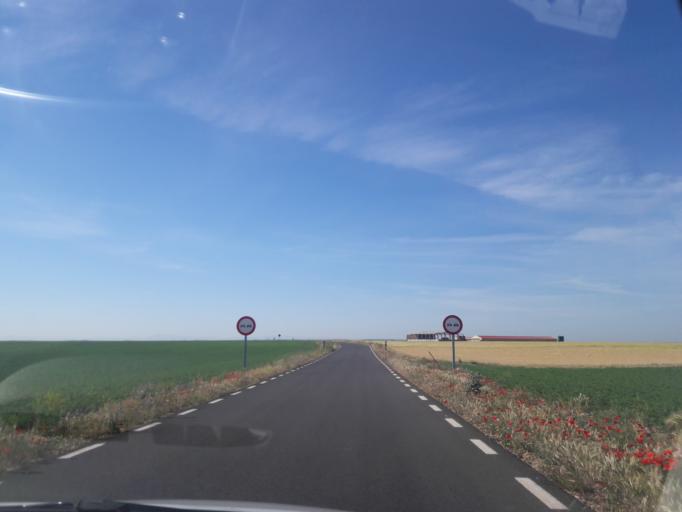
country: ES
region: Castille and Leon
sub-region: Provincia de Salamanca
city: Parada de Rubiales
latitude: 41.1312
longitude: -5.4302
